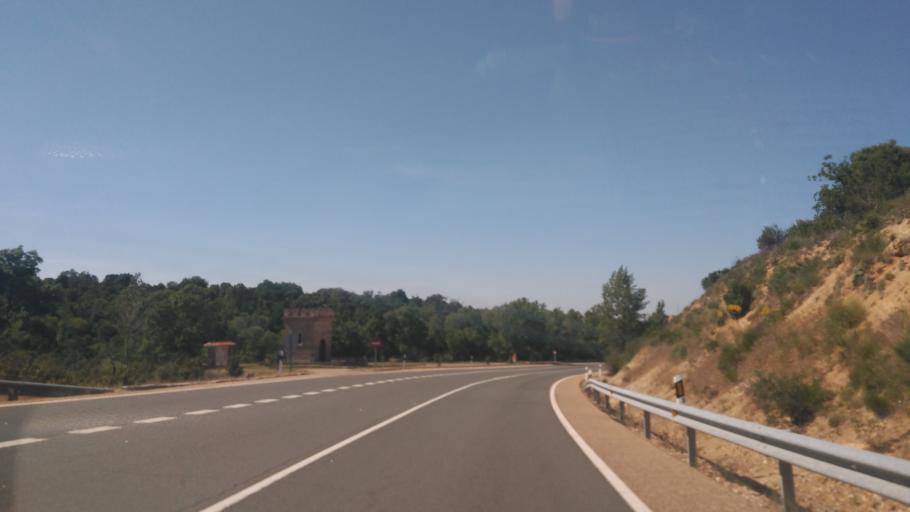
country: ES
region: Castille and Leon
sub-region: Provincia de Zamora
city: Corrales
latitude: 41.3035
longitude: -5.7273
